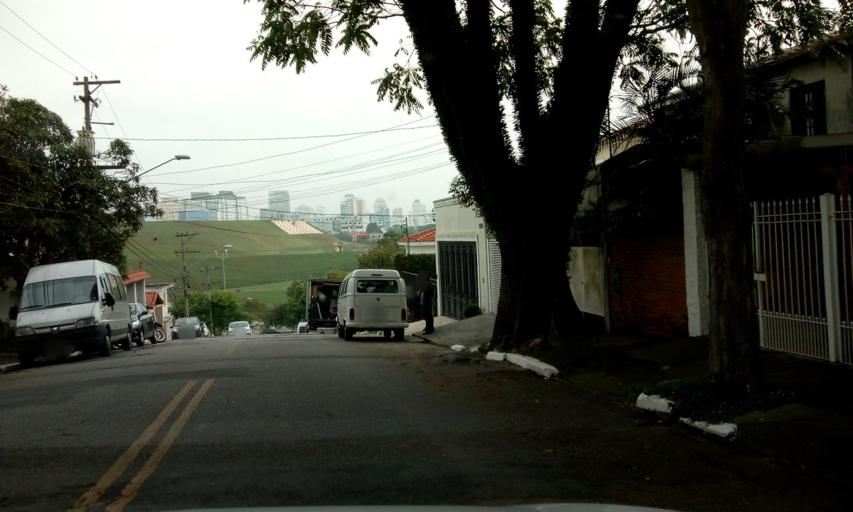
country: BR
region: Sao Paulo
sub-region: Sao Paulo
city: Sao Paulo
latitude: -23.6172
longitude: -46.6585
